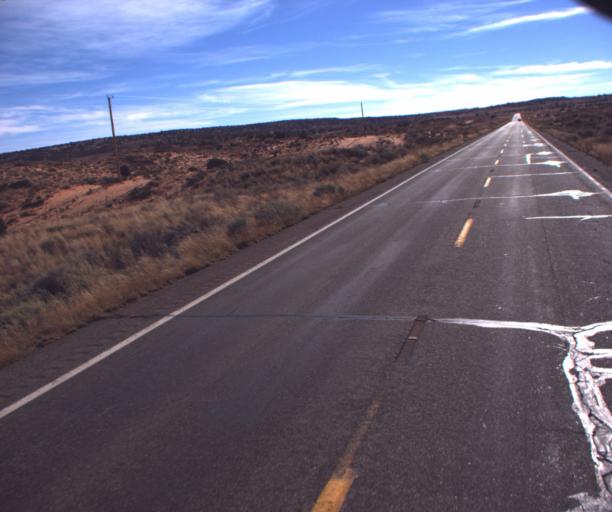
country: US
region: Arizona
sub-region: Coconino County
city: Kaibito
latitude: 36.5908
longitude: -111.1575
